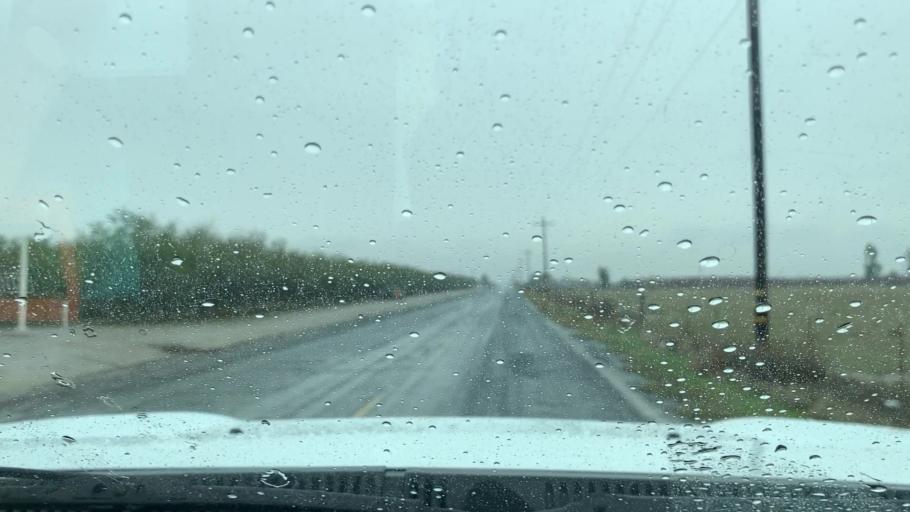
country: US
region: California
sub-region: Tulare County
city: Earlimart
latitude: 35.8919
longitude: -119.3354
